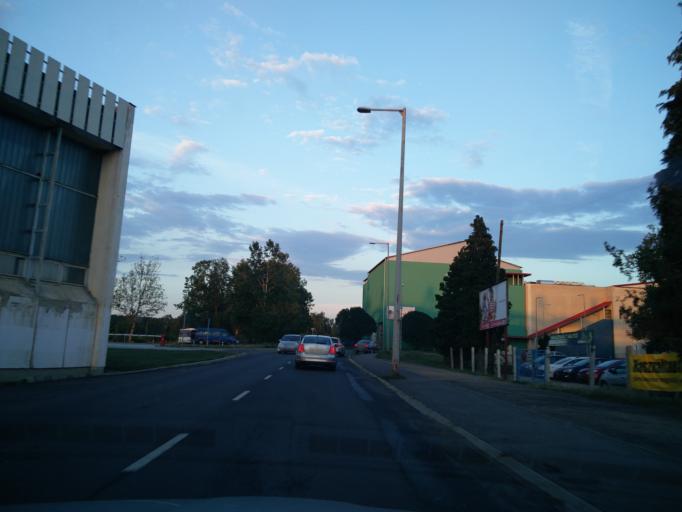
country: HU
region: Zala
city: Zalaegerszeg
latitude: 46.8479
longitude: 16.8499
